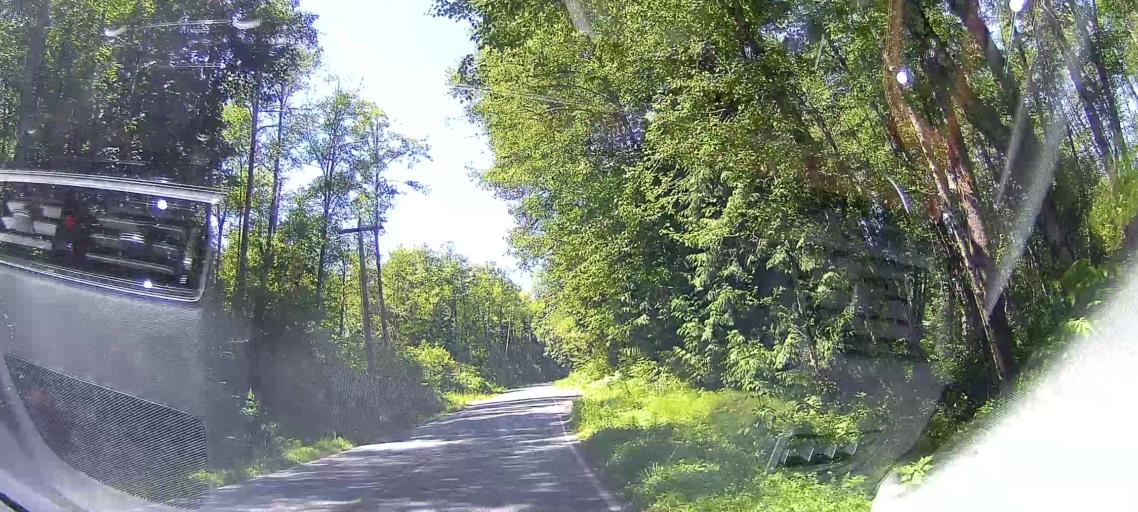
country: US
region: Washington
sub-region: Skagit County
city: Sedro-Woolley
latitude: 48.5845
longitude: -122.2927
